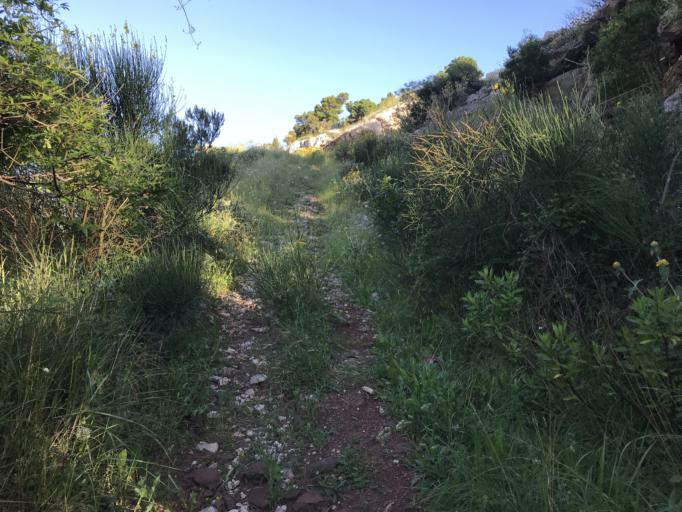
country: ME
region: Bar
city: Sutomore
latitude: 42.1376
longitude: 19.0471
